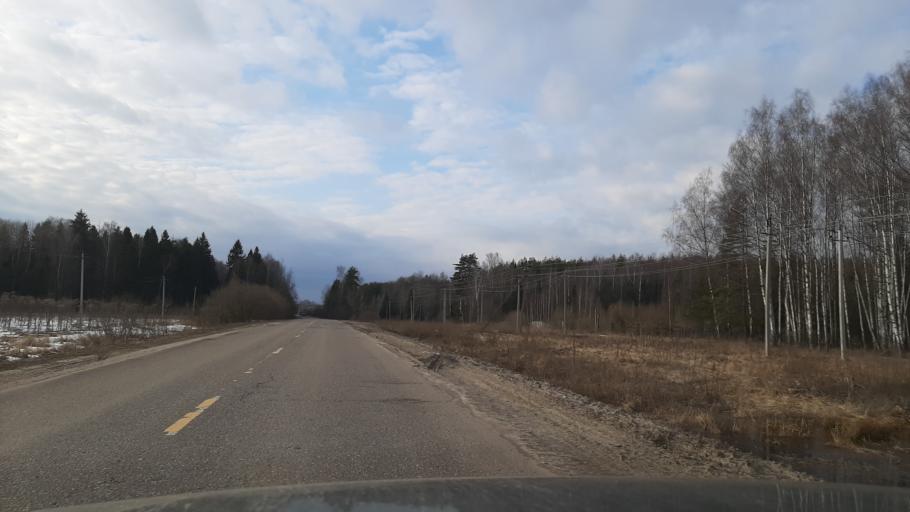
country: RU
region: Ivanovo
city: Novo-Talitsy
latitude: 56.9348
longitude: 40.7326
